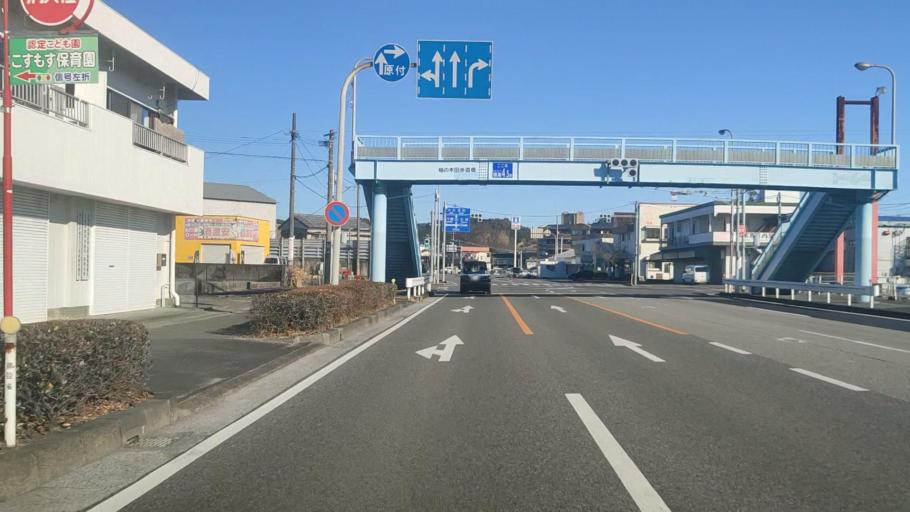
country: JP
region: Miyazaki
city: Nobeoka
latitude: 32.6007
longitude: 131.6824
